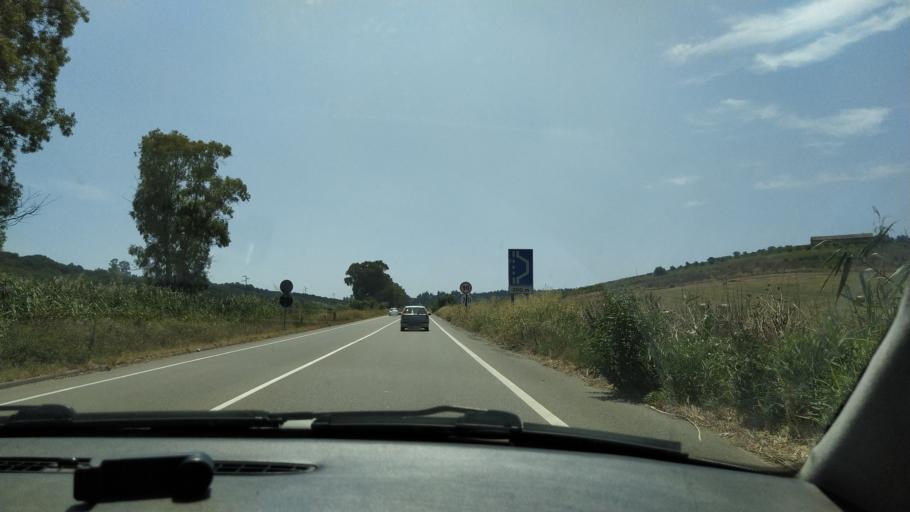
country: IT
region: Basilicate
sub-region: Provincia di Matera
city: Bernalda
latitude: 40.4419
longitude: 16.7824
